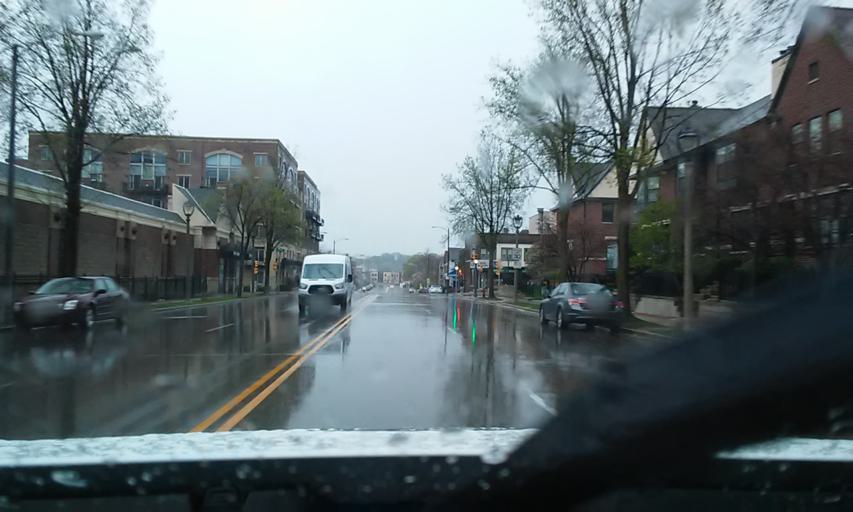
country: US
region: Wisconsin
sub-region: Milwaukee County
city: Milwaukee
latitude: 43.0486
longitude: -87.9035
